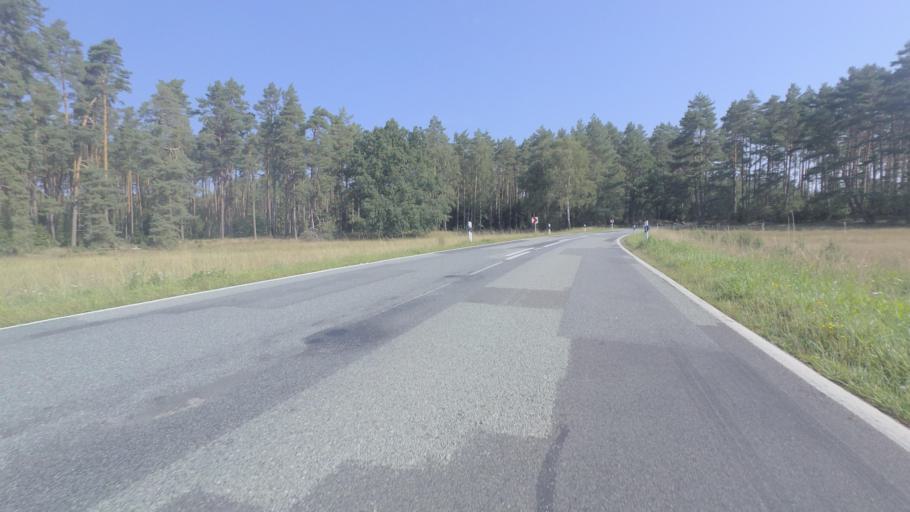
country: DE
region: Mecklenburg-Vorpommern
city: Malchow
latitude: 53.5452
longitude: 12.4344
